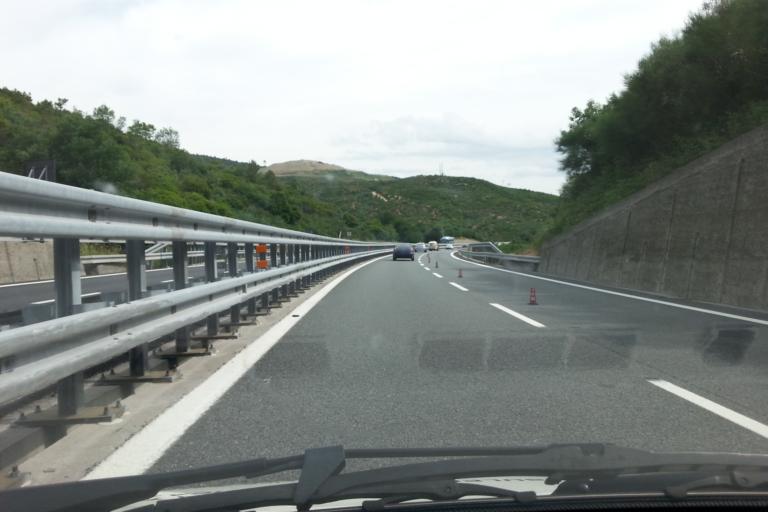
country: IT
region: Liguria
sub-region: Provincia di Savona
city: Valle di Vado
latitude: 44.2604
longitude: 8.4073
